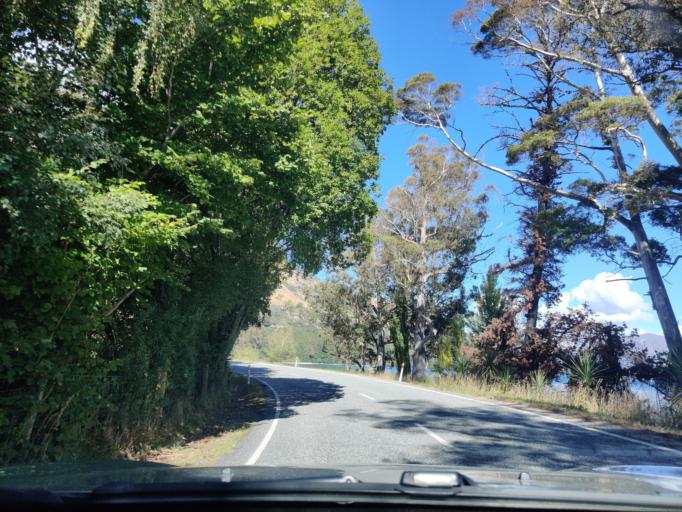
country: NZ
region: Otago
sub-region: Queenstown-Lakes District
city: Queenstown
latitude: -45.0006
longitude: 168.4388
